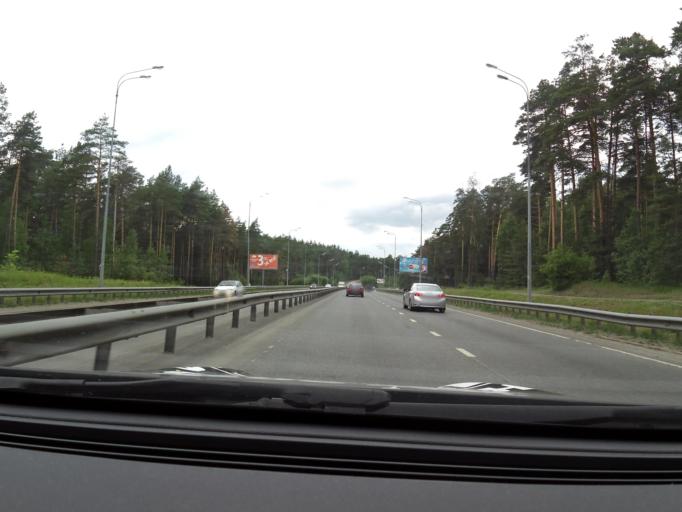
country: RU
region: Tatarstan
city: Staroye Arakchino
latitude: 55.8307
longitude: 48.9919
